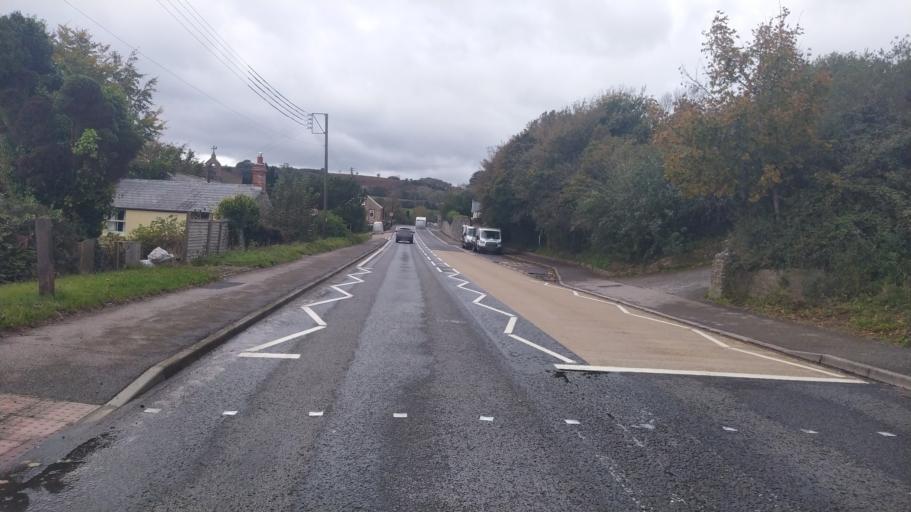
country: GB
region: England
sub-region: Dorset
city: Bridport
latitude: 50.7410
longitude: -2.8433
